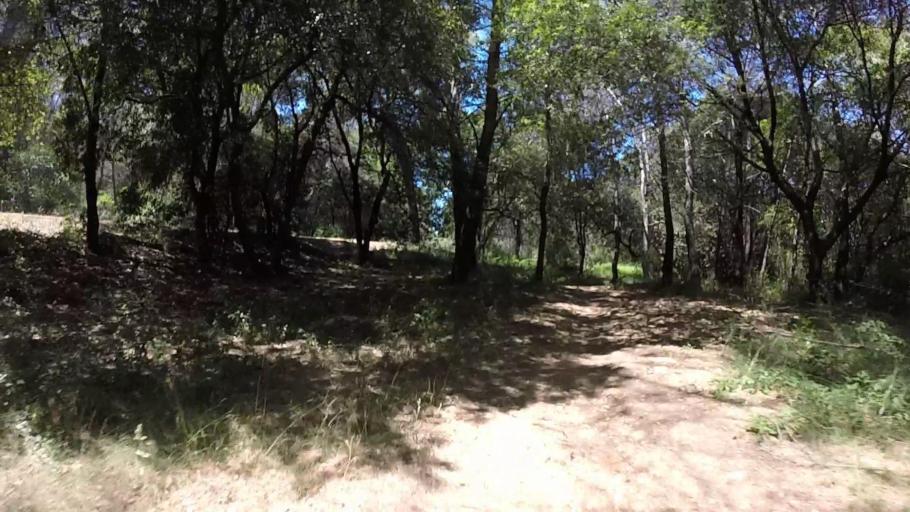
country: FR
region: Provence-Alpes-Cote d'Azur
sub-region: Departement des Alpes-Maritimes
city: Vallauris
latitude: 43.6053
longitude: 7.0485
